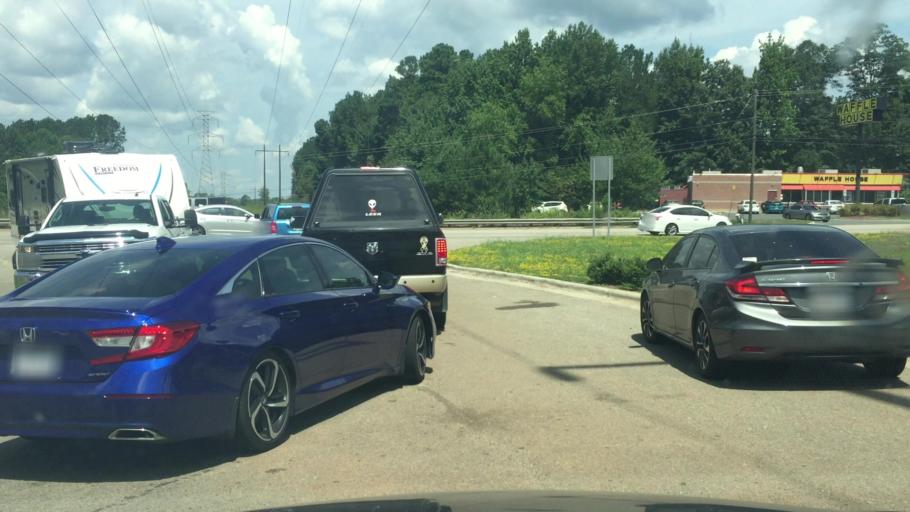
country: US
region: North Carolina
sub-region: Richmond County
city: East Rockingham
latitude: 34.9118
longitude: -79.7903
